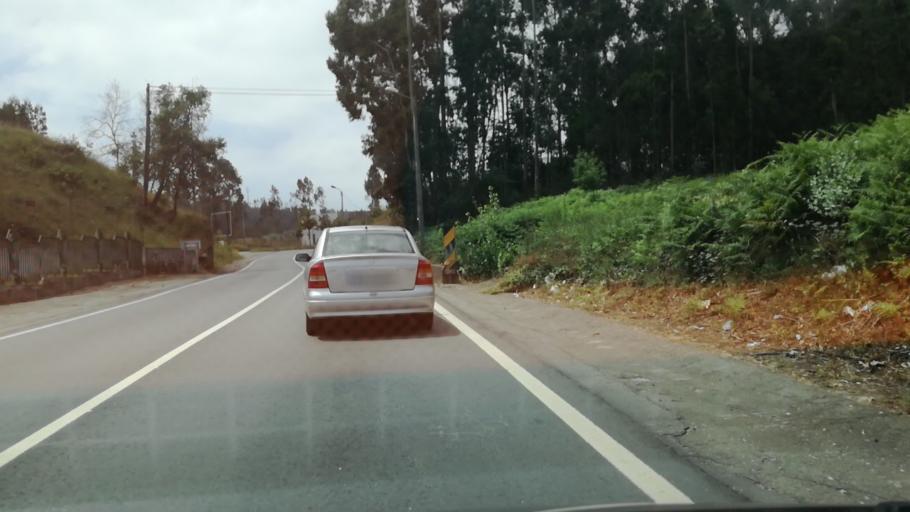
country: PT
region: Porto
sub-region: Trofa
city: Sao Romao do Coronado
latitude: 41.3080
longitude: -8.5817
